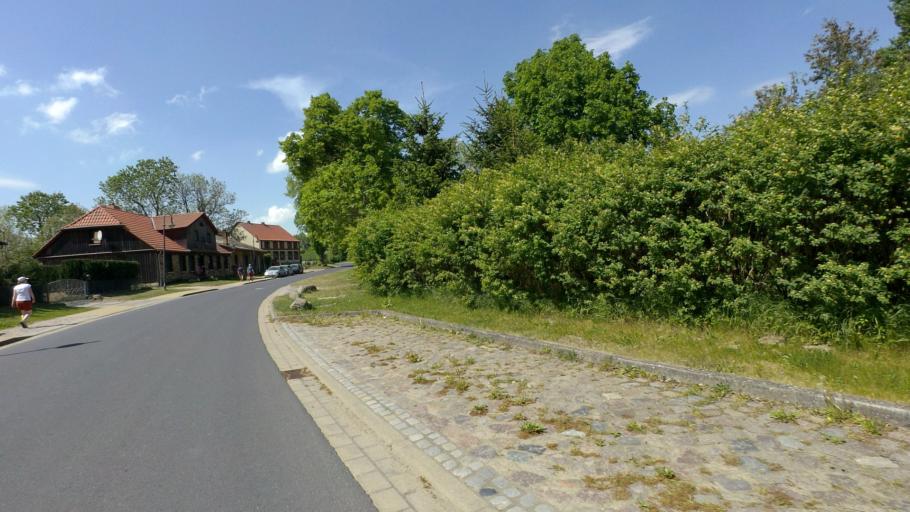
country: DE
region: Mecklenburg-Vorpommern
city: Mollenhagen
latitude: 53.5650
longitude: 12.9128
